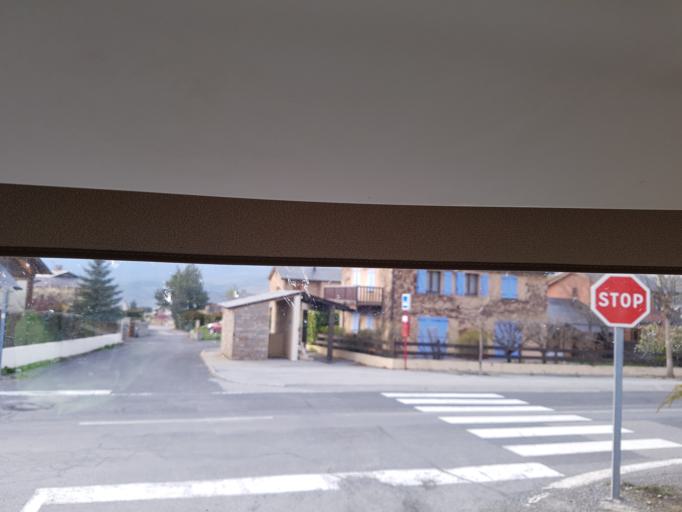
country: ES
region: Catalonia
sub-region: Provincia de Girona
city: Llivia
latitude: 42.4431
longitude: 2.0318
